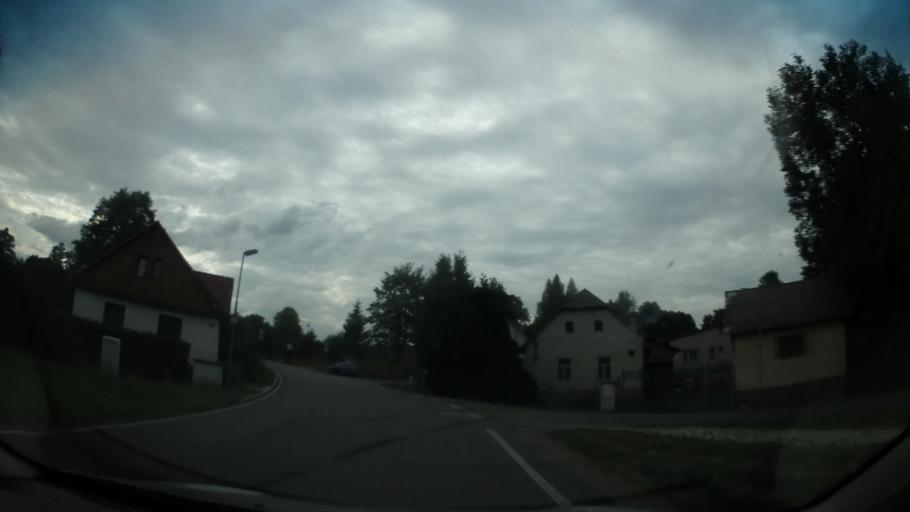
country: CZ
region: Pardubicky
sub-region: Okres Chrudim
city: Nasavrky
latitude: 49.8018
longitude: 15.7725
